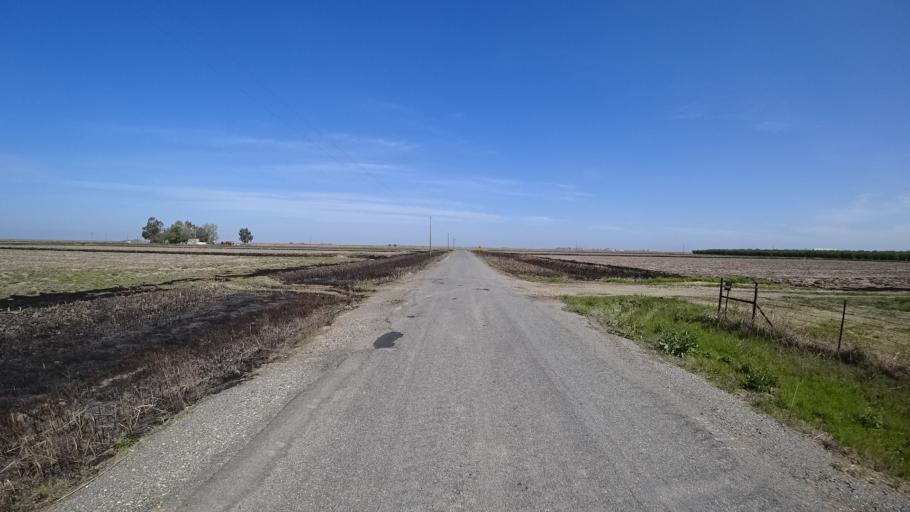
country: US
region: California
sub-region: Glenn County
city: Willows
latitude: 39.5988
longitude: -122.0886
